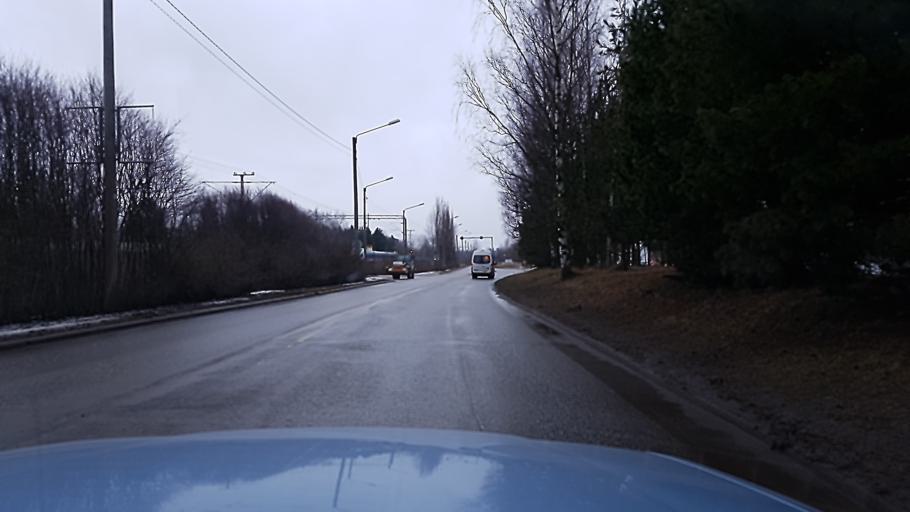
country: FI
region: Uusimaa
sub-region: Helsinki
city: Vantaa
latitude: 60.2728
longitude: 25.0346
